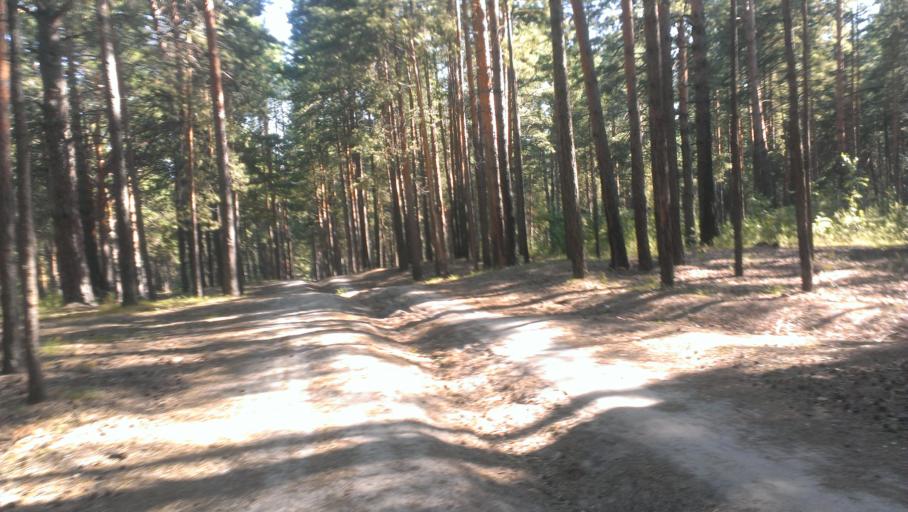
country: RU
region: Altai Krai
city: Novosilikatnyy
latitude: 53.3187
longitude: 83.6863
